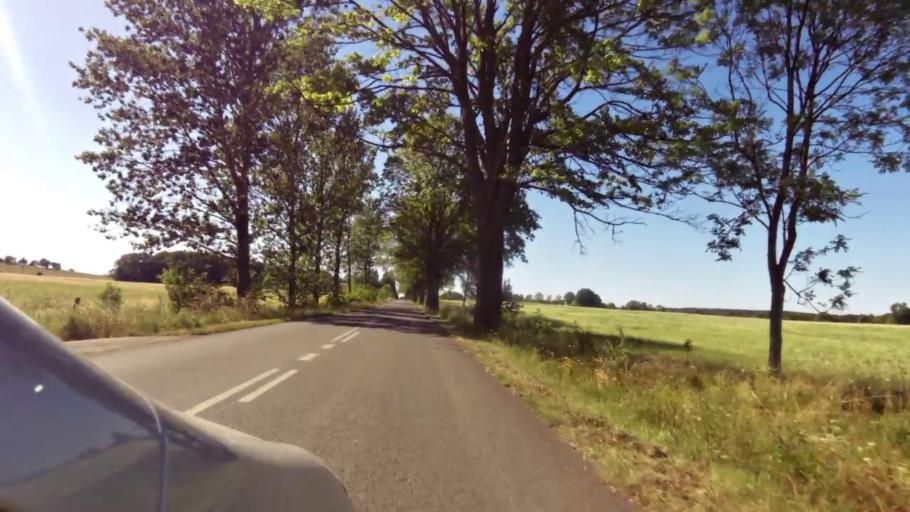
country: PL
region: West Pomeranian Voivodeship
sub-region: Powiat szczecinecki
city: Bialy Bor
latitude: 53.8165
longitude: 16.8229
